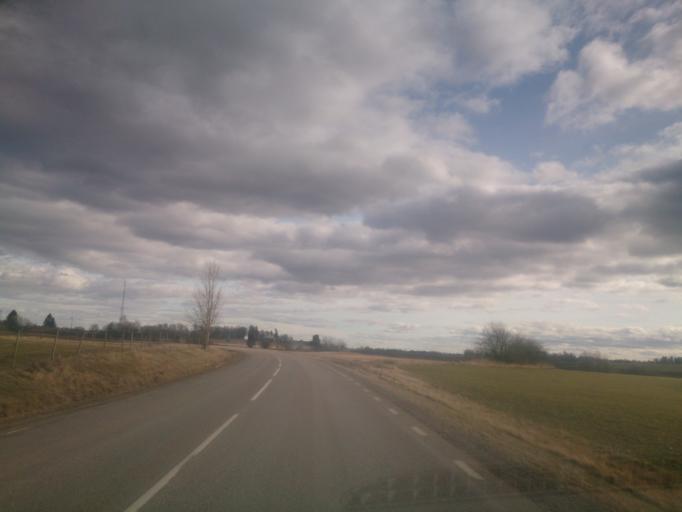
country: SE
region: OEstergoetland
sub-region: Motala Kommun
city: Borensberg
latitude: 58.4814
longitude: 15.2163
